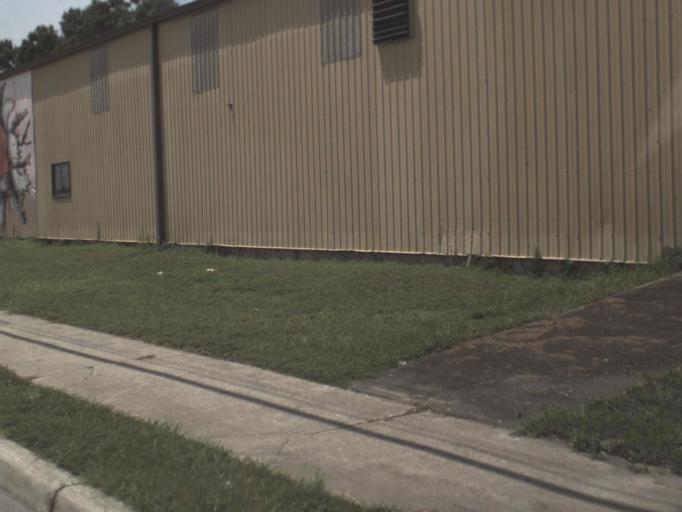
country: US
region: Florida
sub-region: Hillsborough County
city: East Lake-Orient Park
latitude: 27.9684
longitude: -82.4143
